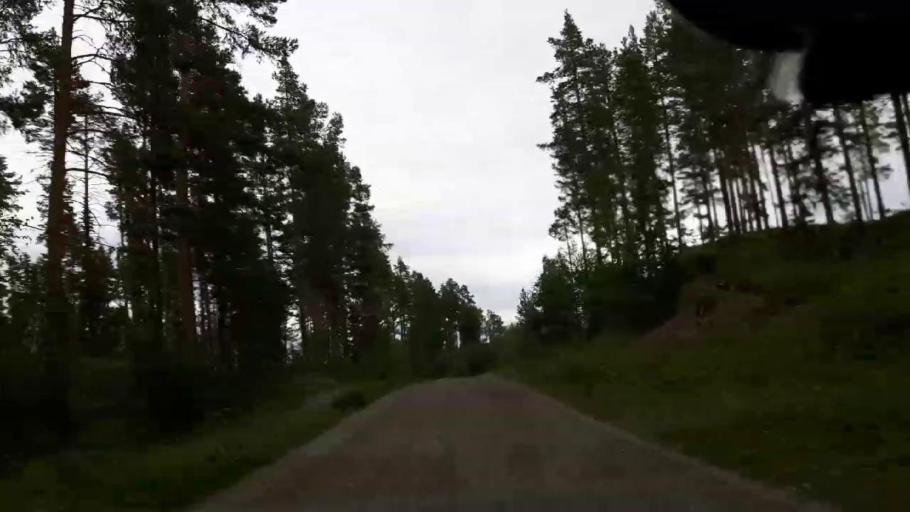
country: SE
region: Jaemtland
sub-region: Braecke Kommun
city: Braecke
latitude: 62.9158
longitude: 15.5736
